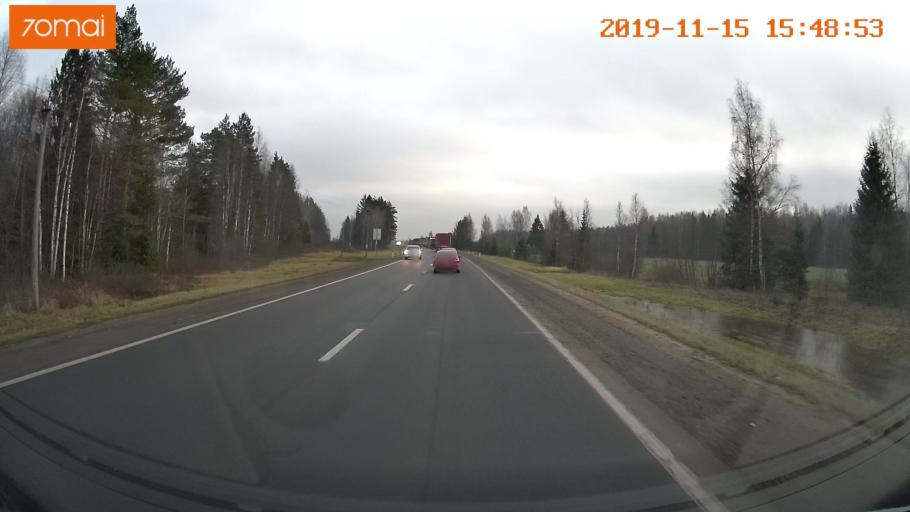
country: RU
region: Jaroslavl
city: Danilov
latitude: 57.9222
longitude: 40.0067
